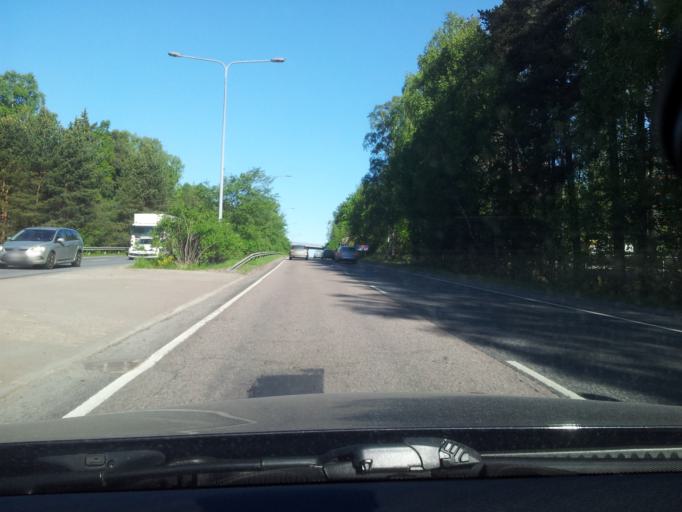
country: FI
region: Uusimaa
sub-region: Helsinki
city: Otaniemi
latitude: 60.1798
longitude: 24.8222
